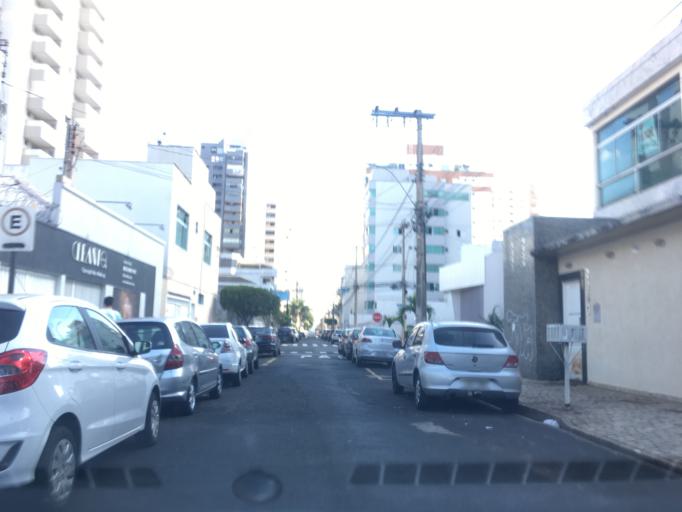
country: BR
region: Minas Gerais
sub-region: Uberlandia
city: Uberlandia
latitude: -18.9166
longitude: -48.2824
